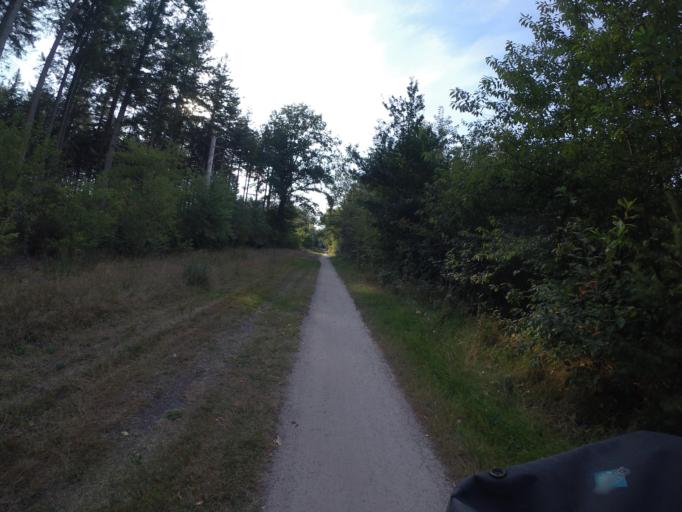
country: NL
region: Drenthe
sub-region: Gemeente Westerveld
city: Dwingeloo
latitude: 52.9194
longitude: 6.3324
